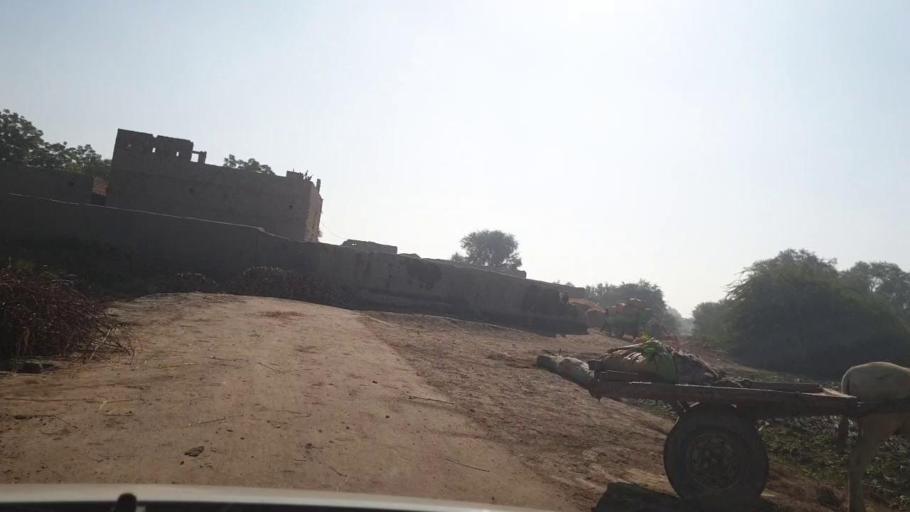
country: PK
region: Sindh
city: Dadu
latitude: 26.6368
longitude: 67.8353
